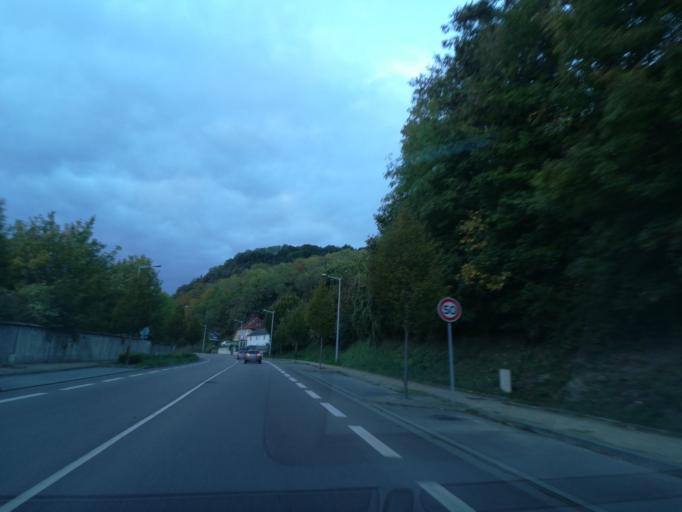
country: FR
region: Haute-Normandie
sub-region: Departement de la Seine-Maritime
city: Amfreville-la-Mi-Voie
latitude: 49.4119
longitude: 1.1217
